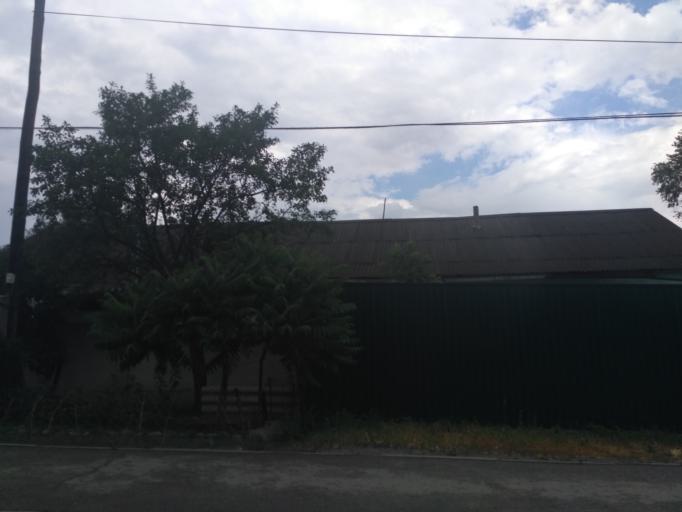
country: KZ
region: Almaty Oblysy
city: Burunday
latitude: 43.2010
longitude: 76.6342
